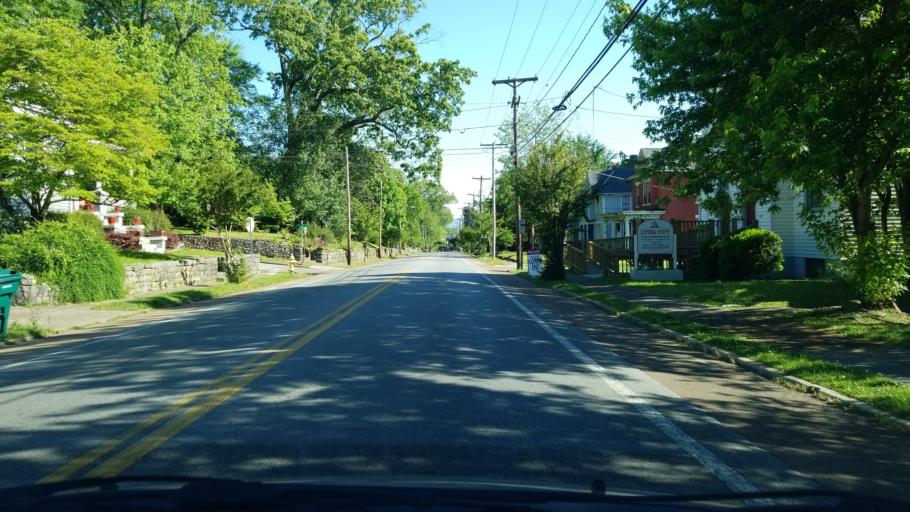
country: US
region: Tennessee
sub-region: Hamilton County
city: Lookout Mountain
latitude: 35.0044
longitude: -85.3289
